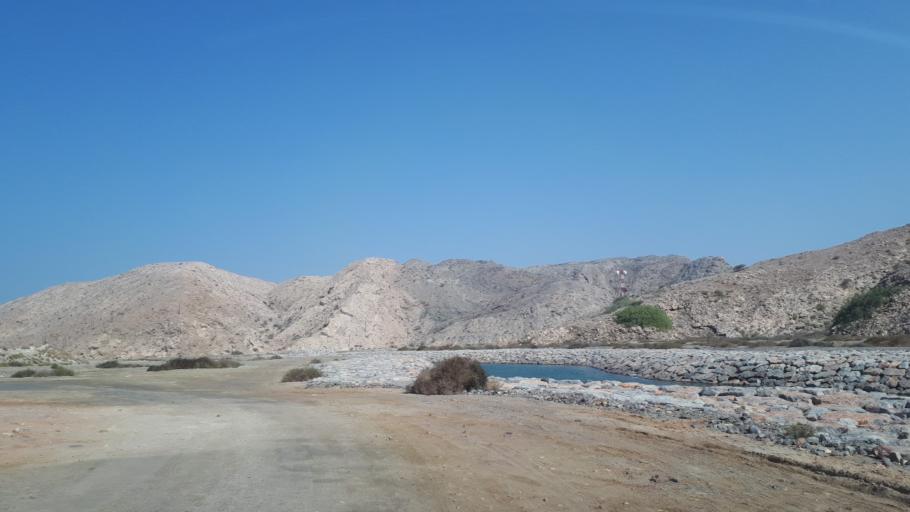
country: OM
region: Muhafazat Masqat
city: Muscat
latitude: 23.5384
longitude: 58.6632
